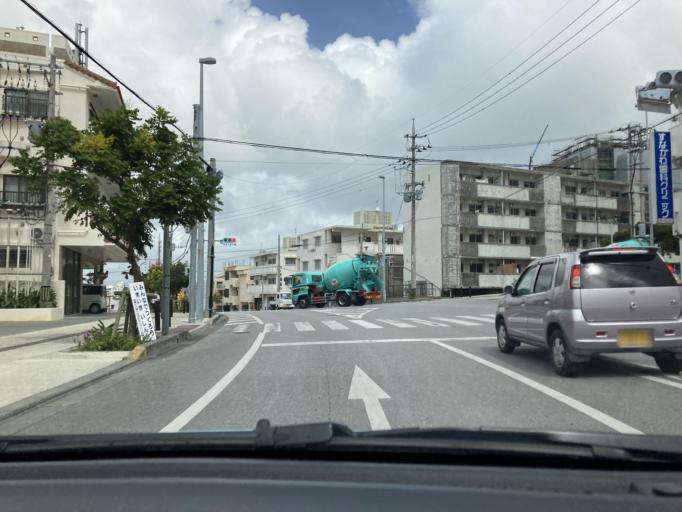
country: JP
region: Okinawa
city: Ginowan
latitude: 26.2281
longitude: 127.7317
